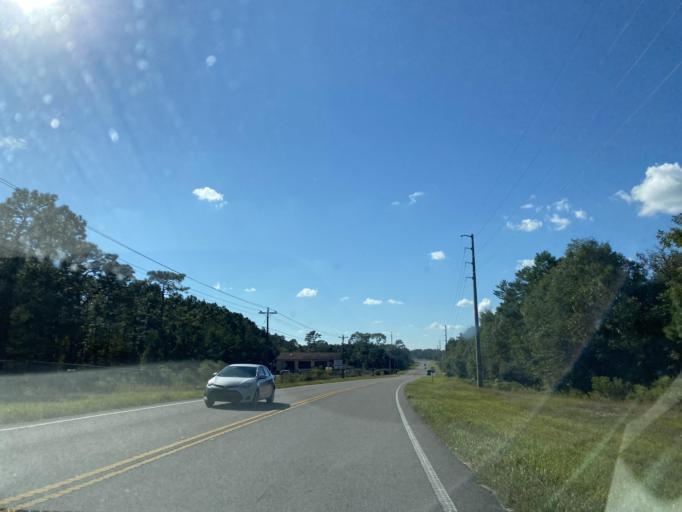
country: US
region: Florida
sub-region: Citrus County
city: Hernando
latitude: 29.0521
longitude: -82.2707
